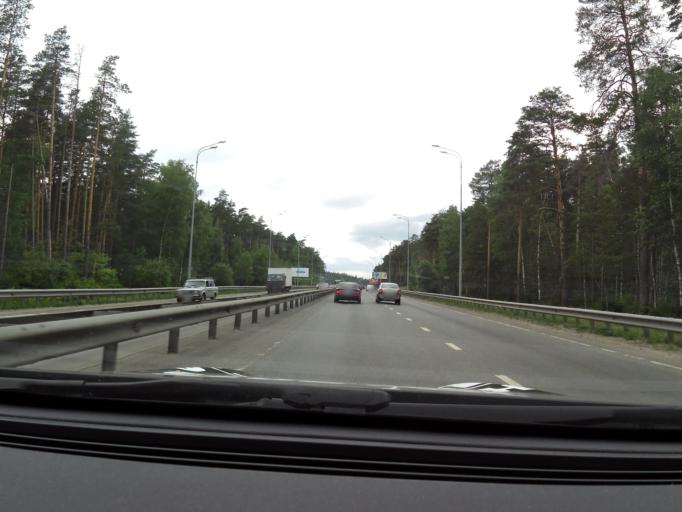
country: RU
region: Tatarstan
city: Staroye Arakchino
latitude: 55.8299
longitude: 48.9990
